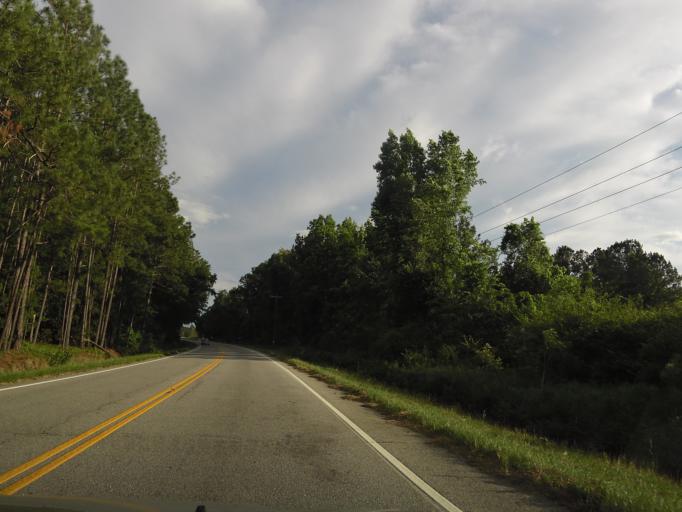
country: US
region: South Carolina
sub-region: Hampton County
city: Estill
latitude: 32.6106
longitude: -81.2447
